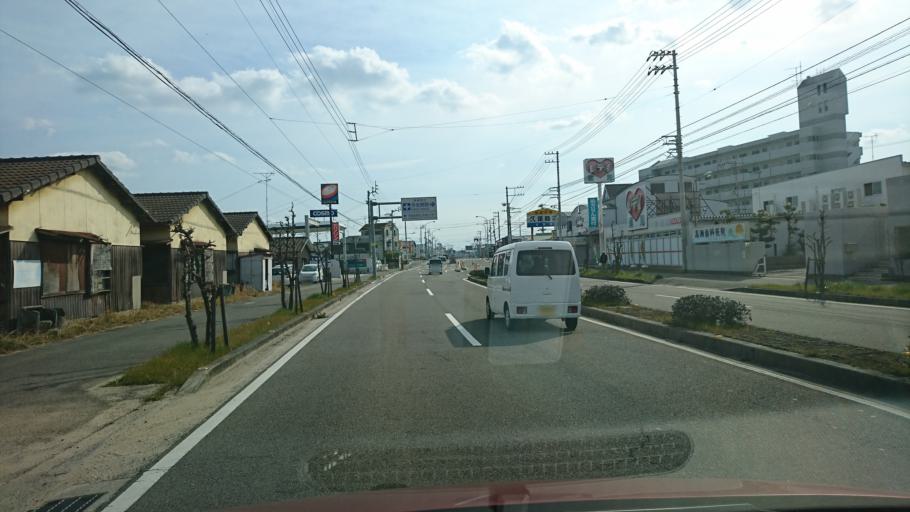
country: JP
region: Ehime
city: Hojo
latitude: 34.0869
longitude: 132.9877
